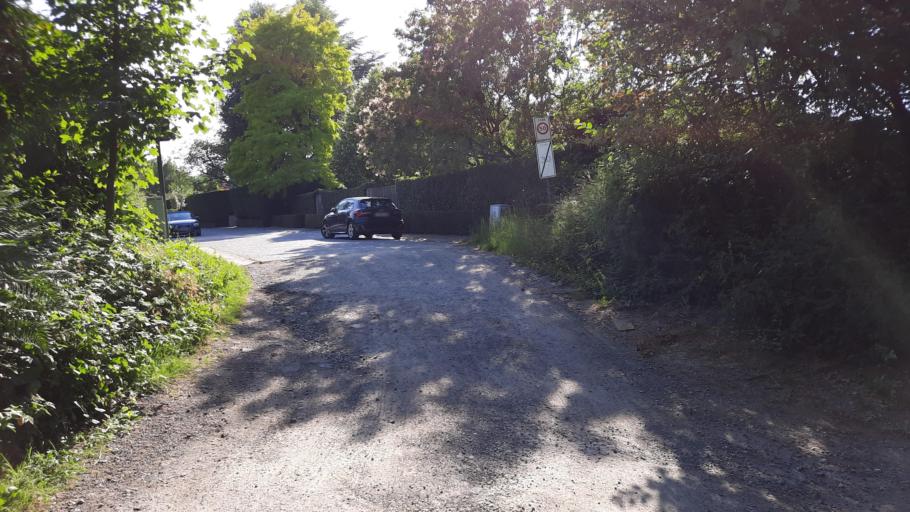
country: BE
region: Flanders
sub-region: Provincie Vlaams-Brabant
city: Wezembeek-Oppem
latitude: 50.8298
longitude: 4.4961
